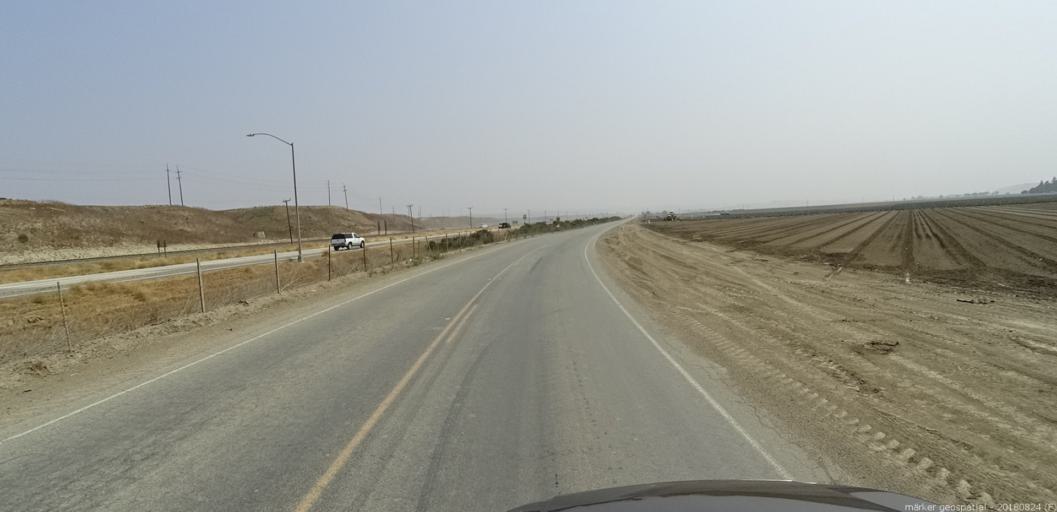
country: US
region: California
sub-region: Monterey County
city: King City
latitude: 36.1997
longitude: -121.1089
